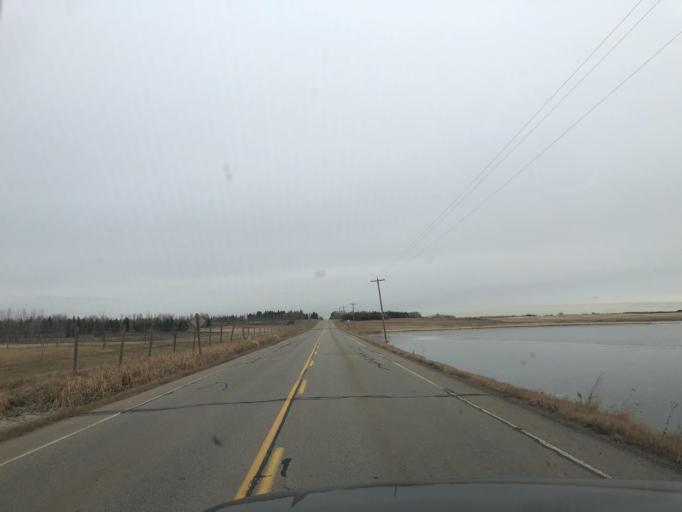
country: CA
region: Alberta
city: Chestermere
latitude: 50.9811
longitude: -113.8654
